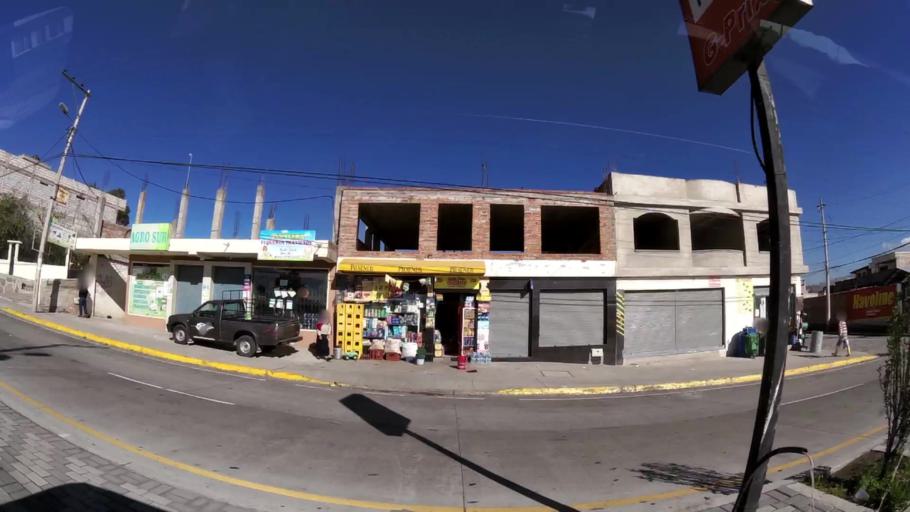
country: EC
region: Chimborazo
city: Riobamba
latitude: -1.6543
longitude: -78.6938
